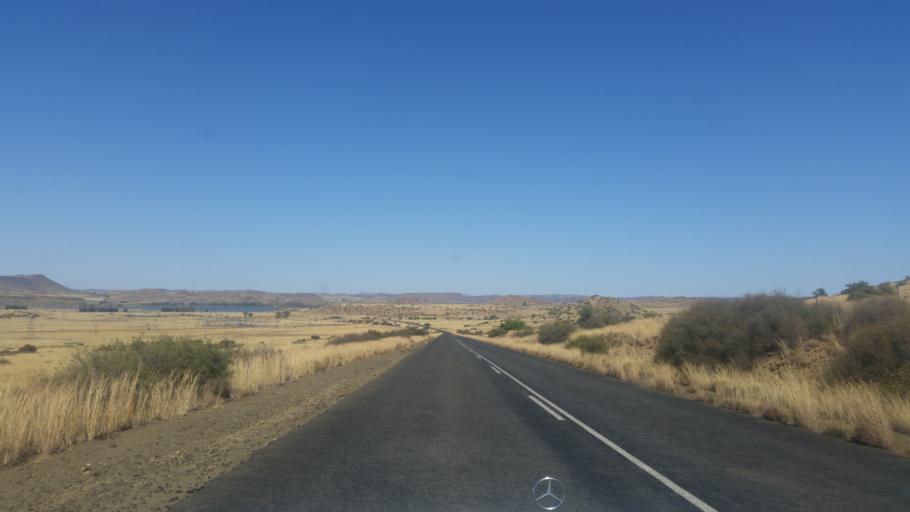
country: ZA
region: Orange Free State
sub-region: Xhariep District Municipality
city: Trompsburg
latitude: -30.4732
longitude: 25.9286
